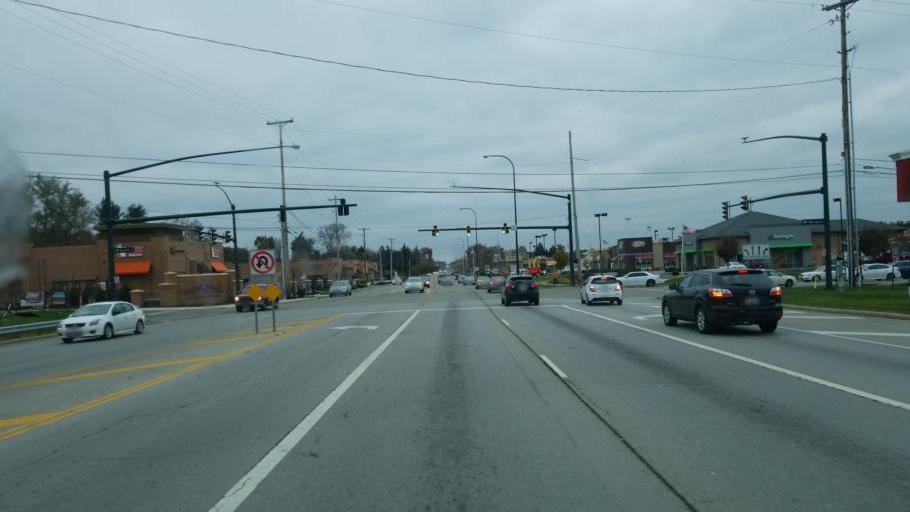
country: US
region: Ohio
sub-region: Franklin County
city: Gahanna
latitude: 40.0090
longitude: -82.8673
